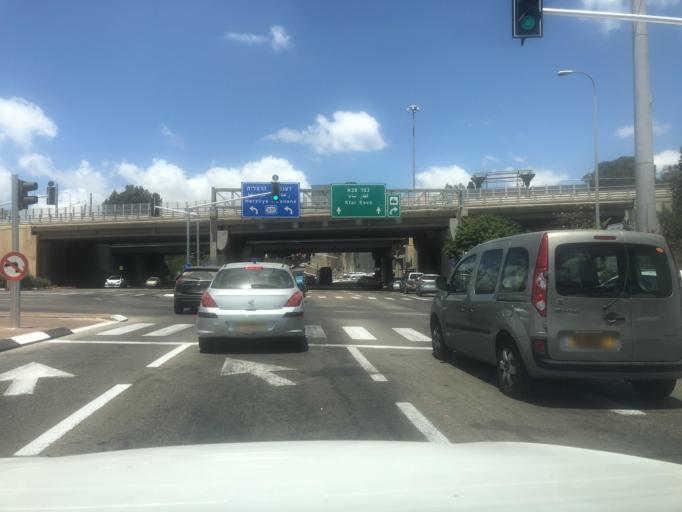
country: IL
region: Central District
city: Kfar Saba
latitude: 32.1695
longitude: 34.9010
